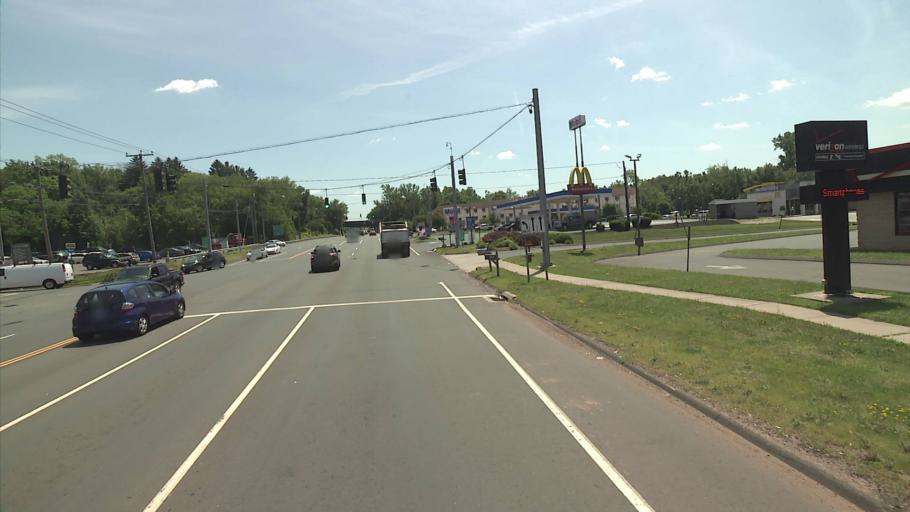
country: US
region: Connecticut
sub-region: Middlesex County
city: Cromwell
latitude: 41.6052
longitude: -72.7075
